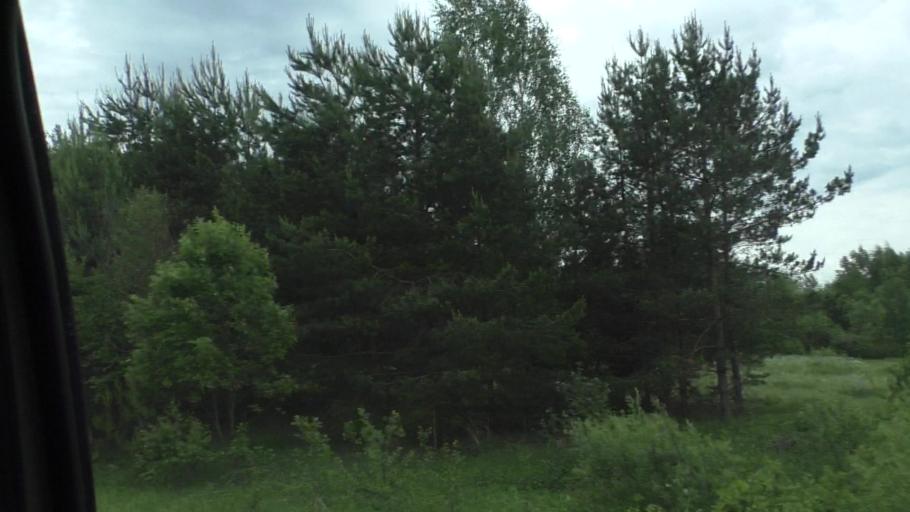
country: RU
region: Moskovskaya
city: Il'inskiy Pogost
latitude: 55.5007
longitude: 38.8028
